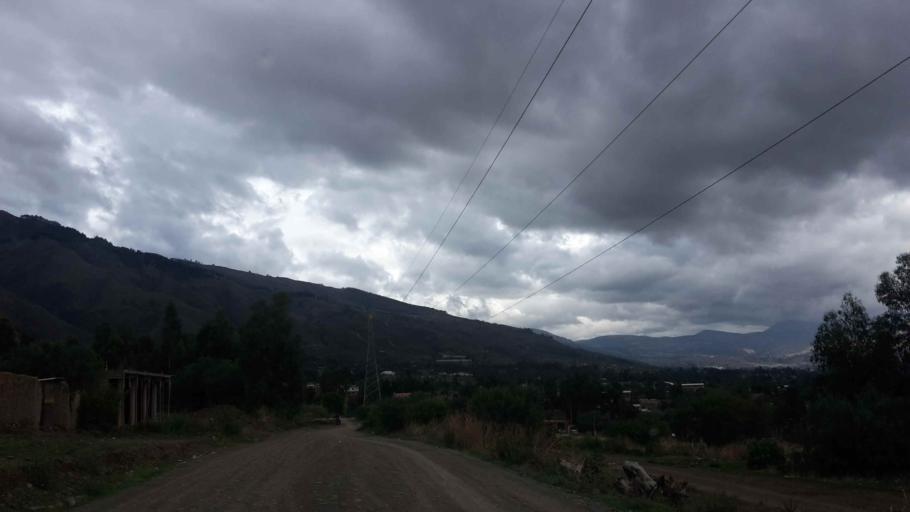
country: BO
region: Cochabamba
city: Cochabamba
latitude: -17.3777
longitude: -66.0594
